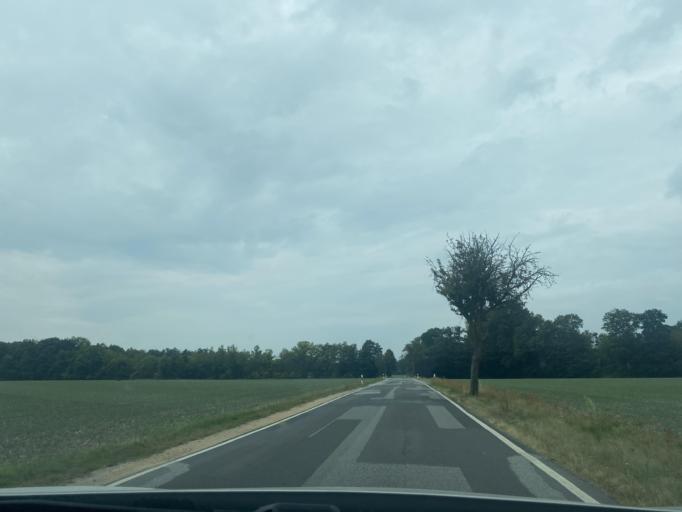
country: DE
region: Saxony
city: Grossdubrau
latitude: 51.2842
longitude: 14.4953
